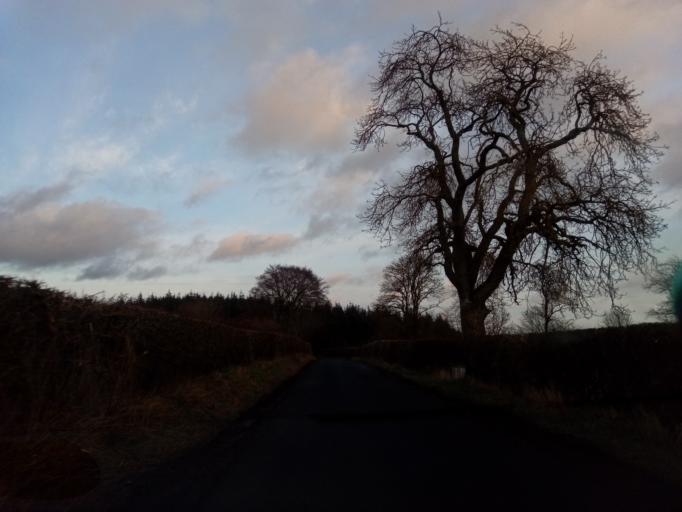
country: GB
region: Scotland
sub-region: The Scottish Borders
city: Newtown St Boswells
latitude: 55.5500
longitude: -2.6957
